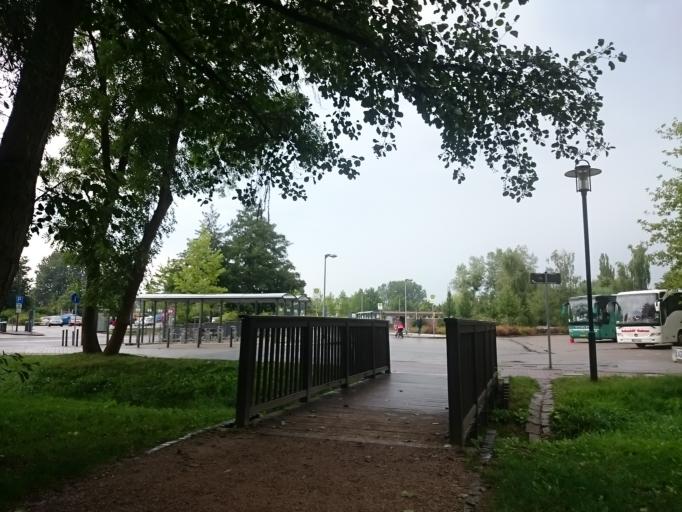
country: DE
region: Mecklenburg-Vorpommern
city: Waren
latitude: 53.5150
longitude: 12.6819
